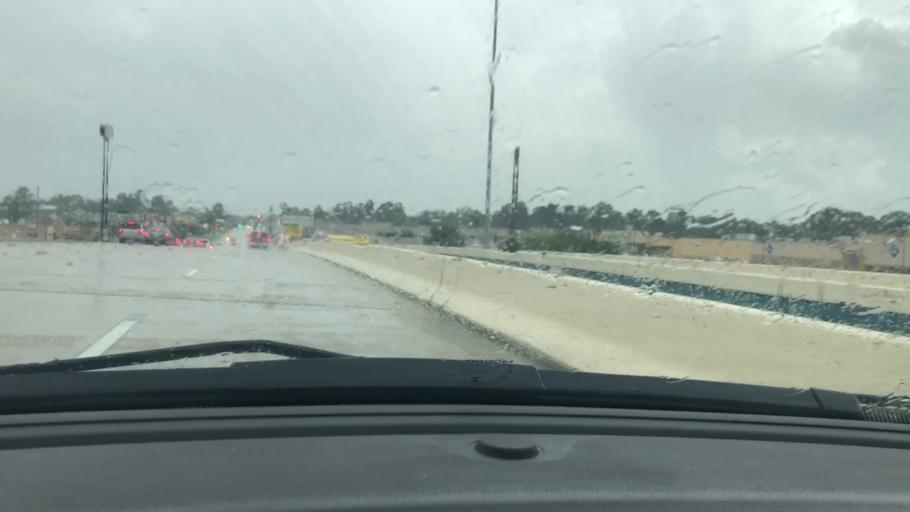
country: US
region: Texas
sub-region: Bowie County
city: Wake Village
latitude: 33.4564
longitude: -94.0867
